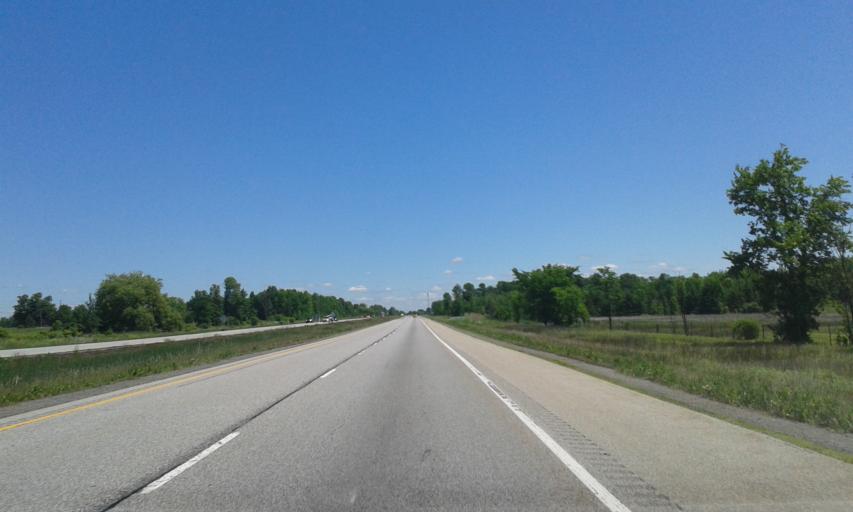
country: US
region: New York
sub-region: St. Lawrence County
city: Ogdensburg
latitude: 44.8799
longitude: -75.2862
